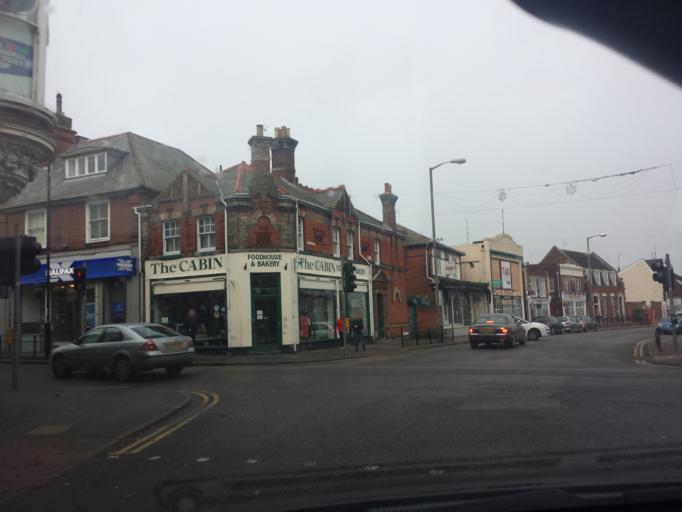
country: GB
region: England
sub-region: Essex
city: Dovercourt
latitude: 51.9369
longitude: 1.2806
